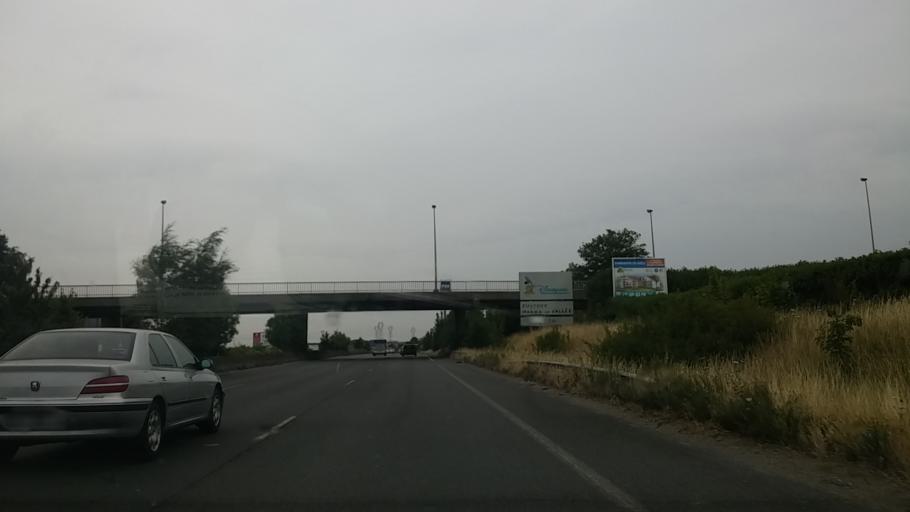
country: FR
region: Ile-de-France
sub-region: Departement de Seine-Saint-Denis
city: Tremblay-en-France
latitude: 48.9682
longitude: 2.5651
